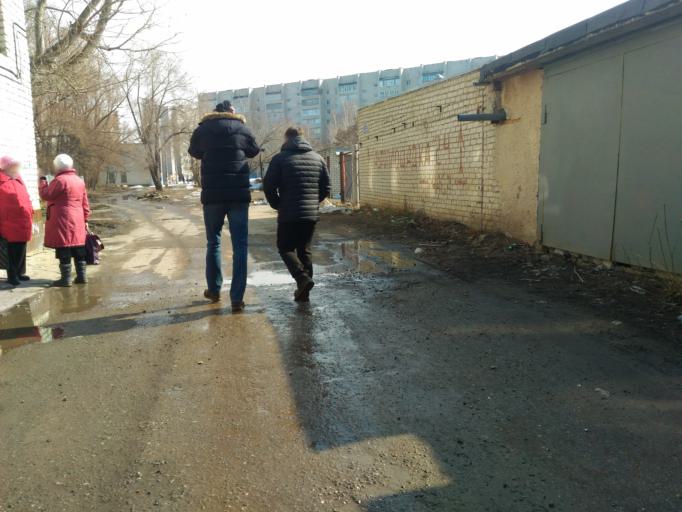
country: RU
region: Ulyanovsk
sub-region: Ulyanovskiy Rayon
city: Ulyanovsk
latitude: 54.3267
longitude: 48.4827
